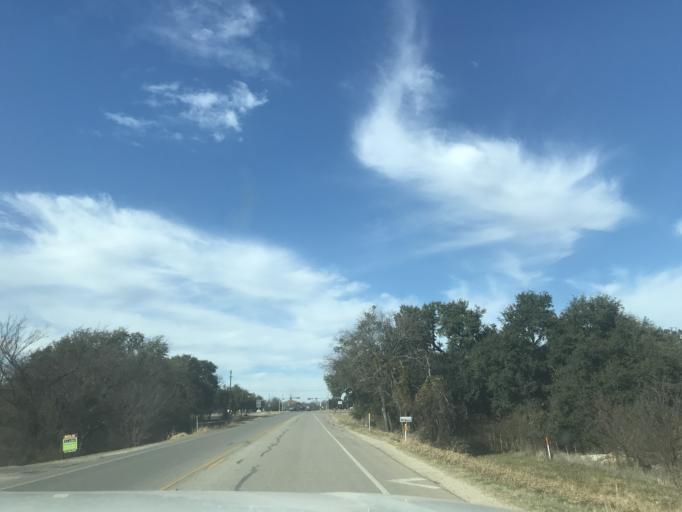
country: US
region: Texas
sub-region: Erath County
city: Stephenville
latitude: 32.2096
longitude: -98.1946
